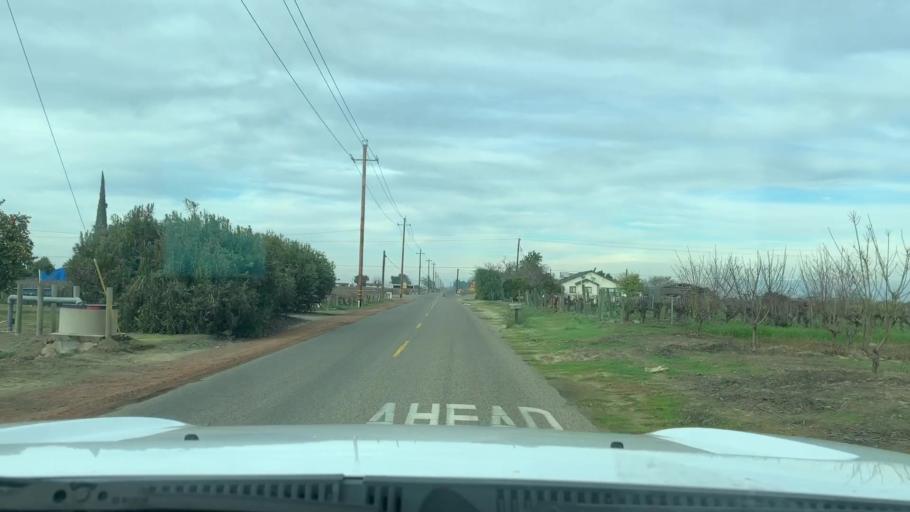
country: US
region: California
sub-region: Fresno County
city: Selma
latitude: 36.5674
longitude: -119.5750
